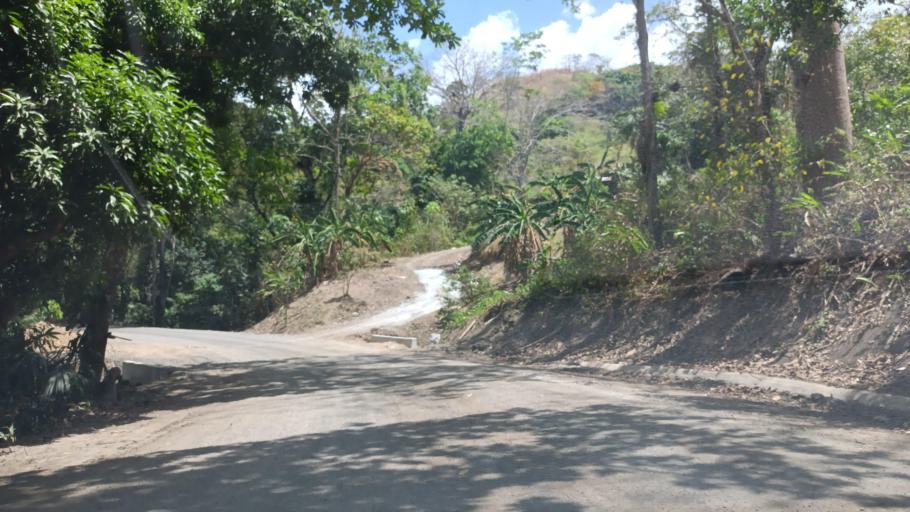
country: PA
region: Panama
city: Las Cumbres
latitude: 9.0738
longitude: -79.5687
